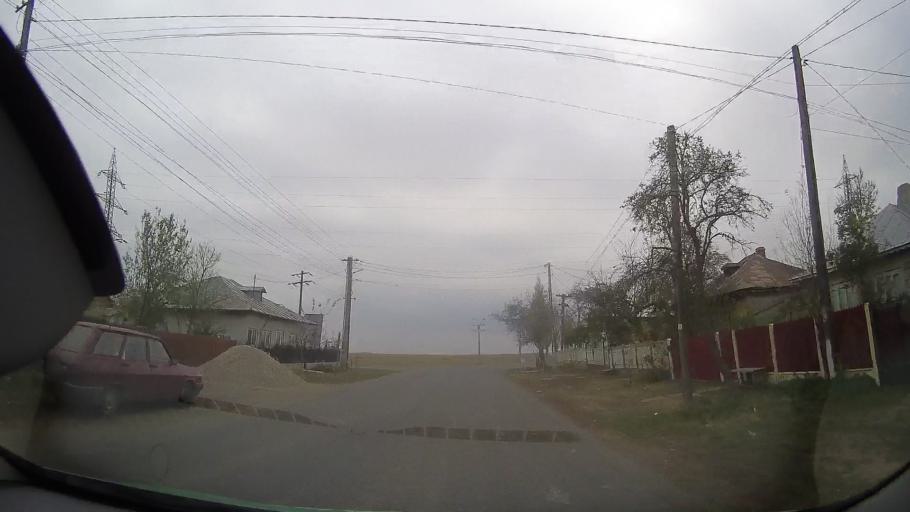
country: RO
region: Buzau
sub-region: Comuna Pogoanele
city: Pogoanele
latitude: 44.9028
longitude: 26.9783
